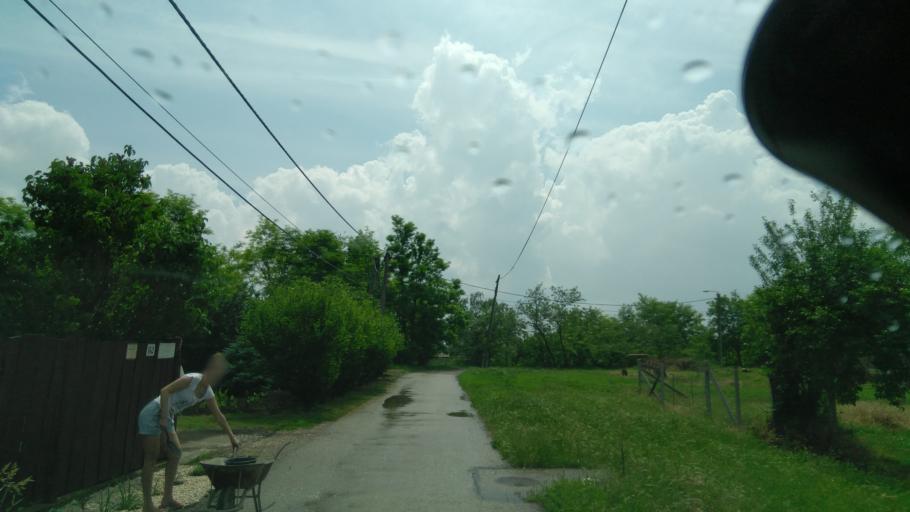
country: HU
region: Bekes
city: Bekescsaba
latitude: 46.6604
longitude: 21.1696
